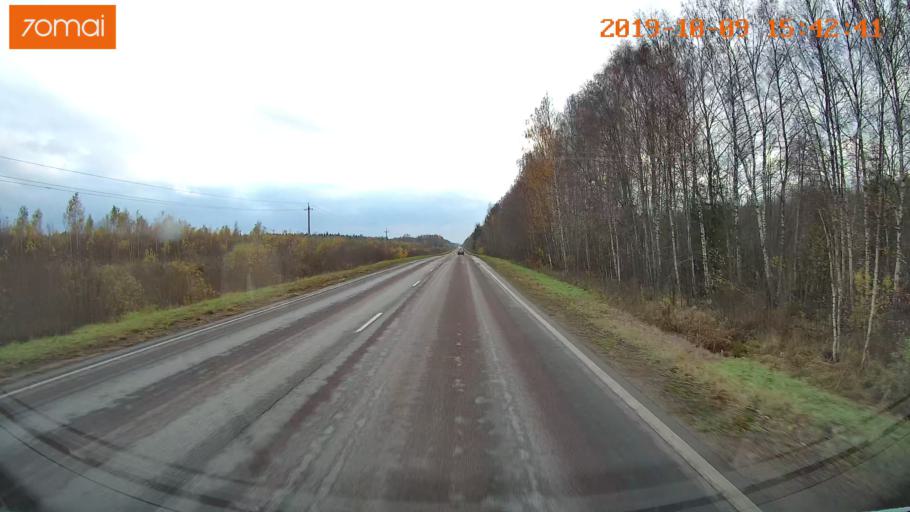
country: RU
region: Kostroma
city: Oktyabr'skiy
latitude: 57.8657
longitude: 41.1022
